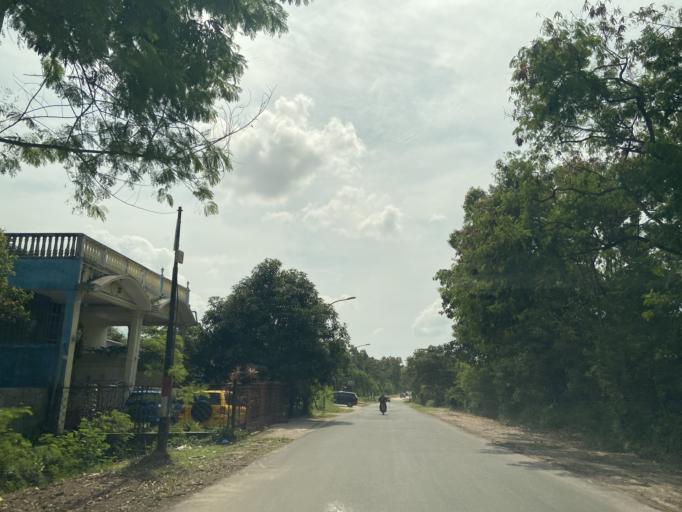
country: SG
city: Singapore
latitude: 1.1274
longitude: 104.0472
